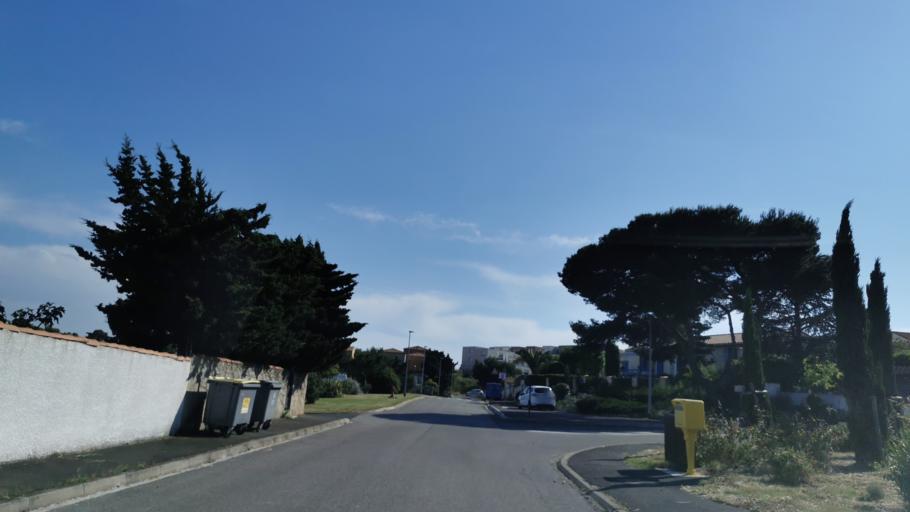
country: FR
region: Languedoc-Roussillon
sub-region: Departement de l'Aude
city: Narbonne
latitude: 43.1419
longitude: 2.9675
